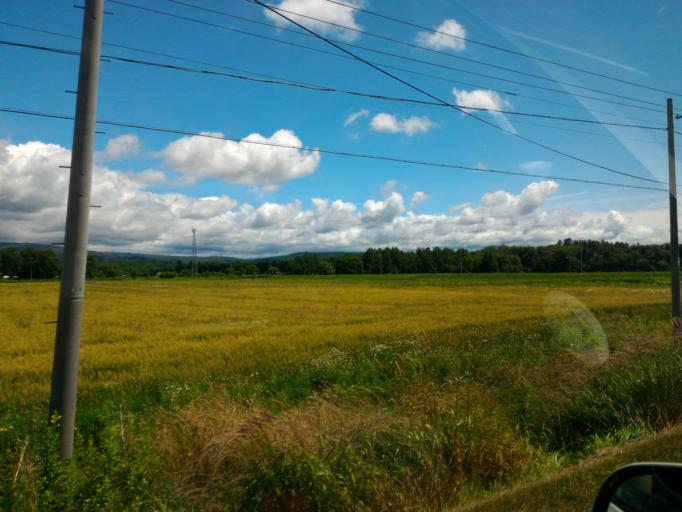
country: JP
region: Hokkaido
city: Nayoro
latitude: 44.5139
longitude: 142.3309
